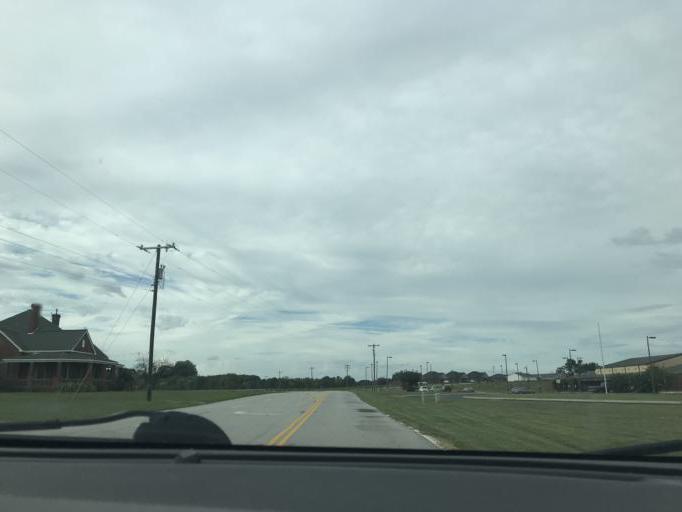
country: US
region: South Carolina
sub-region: Cherokee County
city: East Gaffney
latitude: 35.1326
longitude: -81.6676
